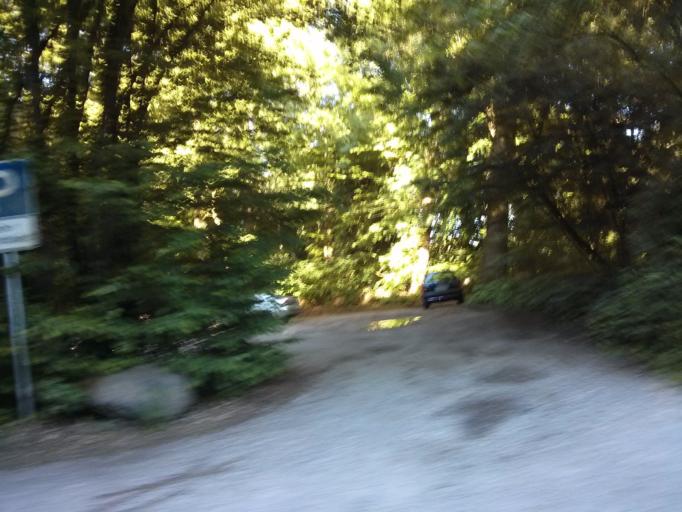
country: DE
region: Hamburg
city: Stellingen
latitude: 53.6077
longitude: 9.9279
